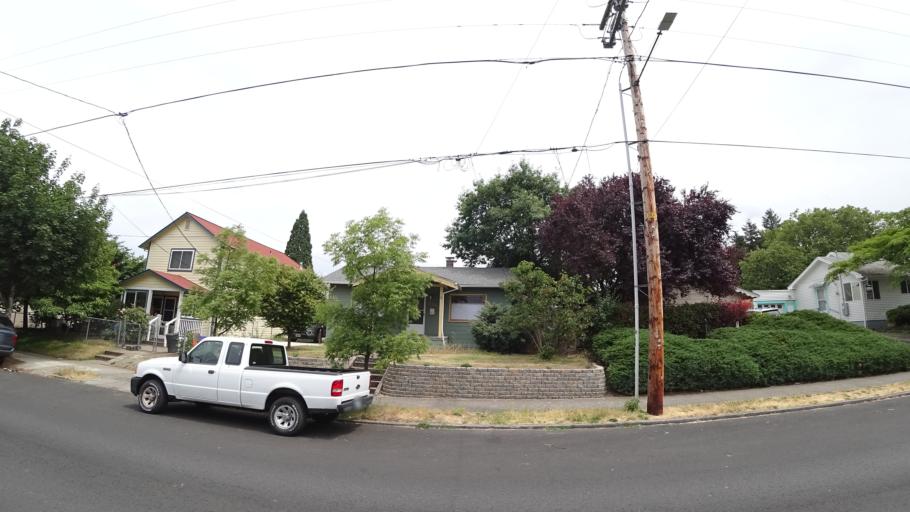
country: US
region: Oregon
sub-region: Multnomah County
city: Portland
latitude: 45.5765
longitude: -122.6956
